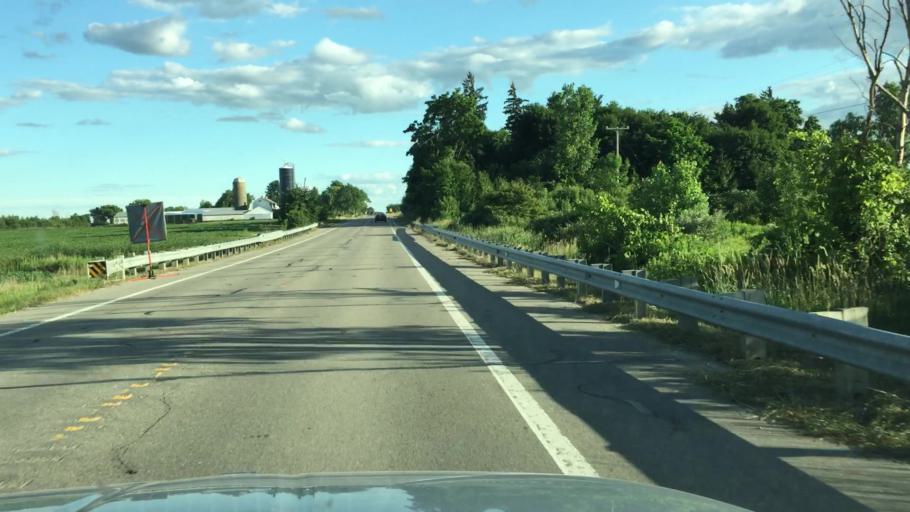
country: US
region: Michigan
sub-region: Saint Clair County
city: Yale
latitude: 43.0937
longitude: -82.7665
